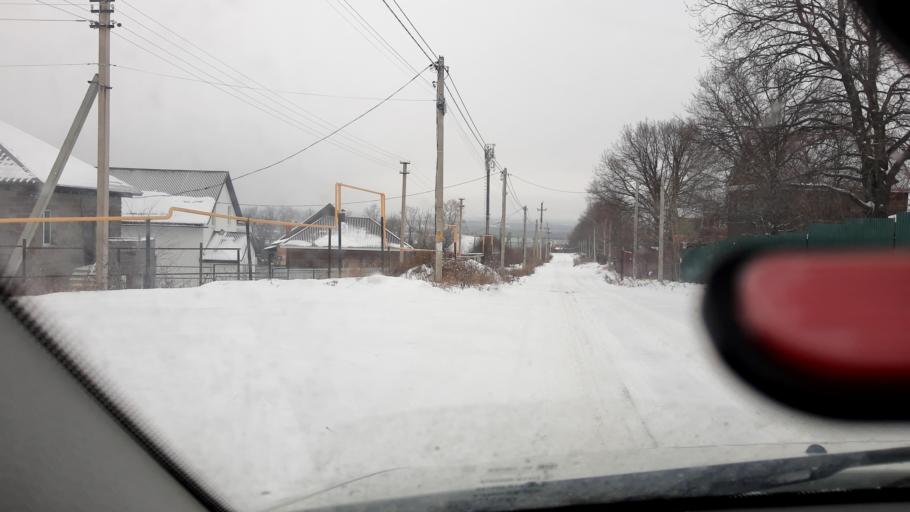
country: RU
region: Bashkortostan
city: Kabakovo
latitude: 54.6305
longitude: 56.0815
